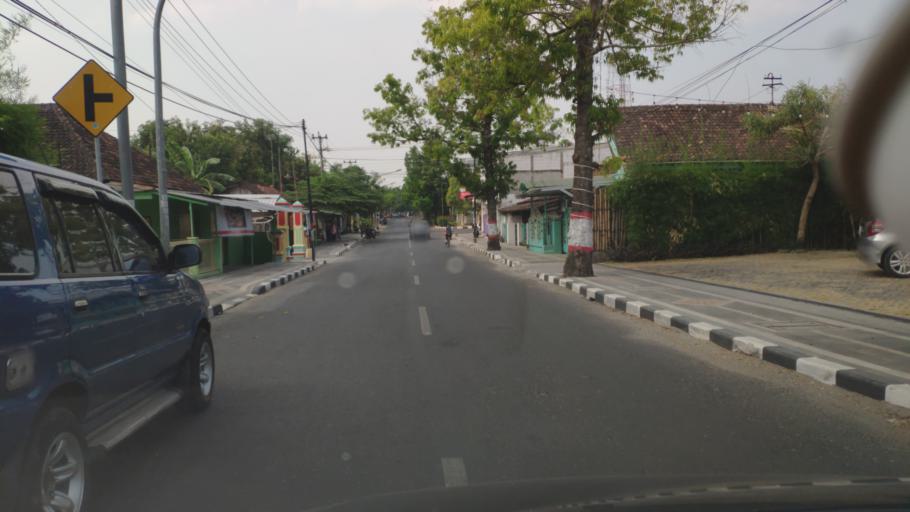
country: ID
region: Central Java
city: Tempelan
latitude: -6.9666
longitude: 111.4129
